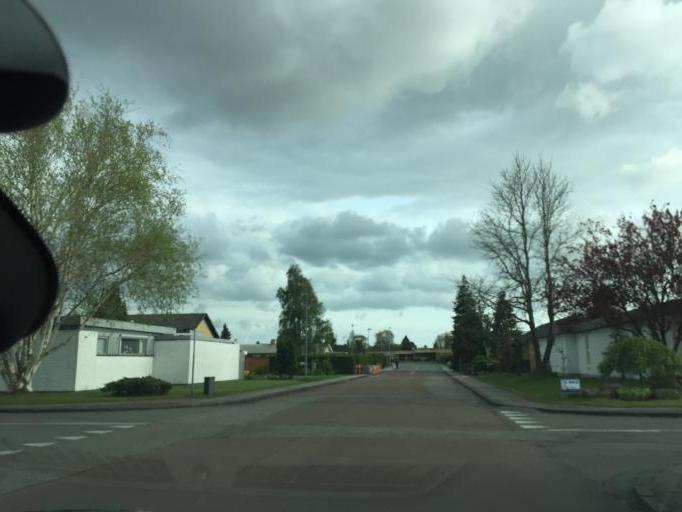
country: DK
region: South Denmark
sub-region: Odense Kommune
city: Odense
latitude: 55.4114
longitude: 10.3416
